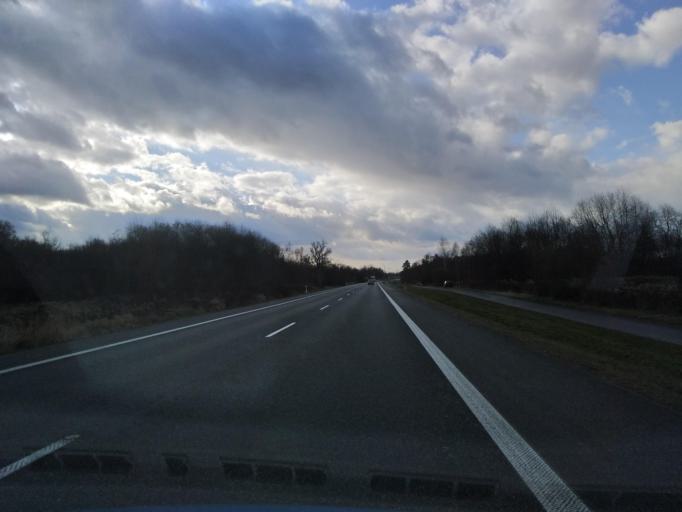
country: PL
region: Lesser Poland Voivodeship
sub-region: Powiat gorlicki
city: Biecz
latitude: 49.7277
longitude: 21.2657
